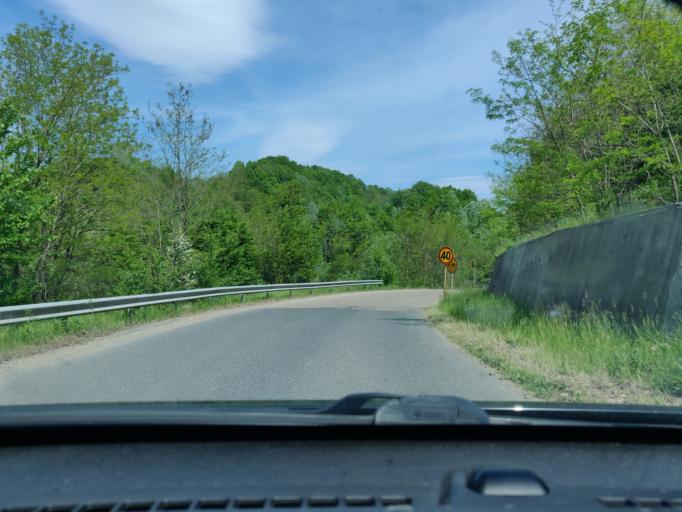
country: RO
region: Vrancea
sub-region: Comuna Vidra
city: Vidra
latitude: 45.9358
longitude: 26.8817
